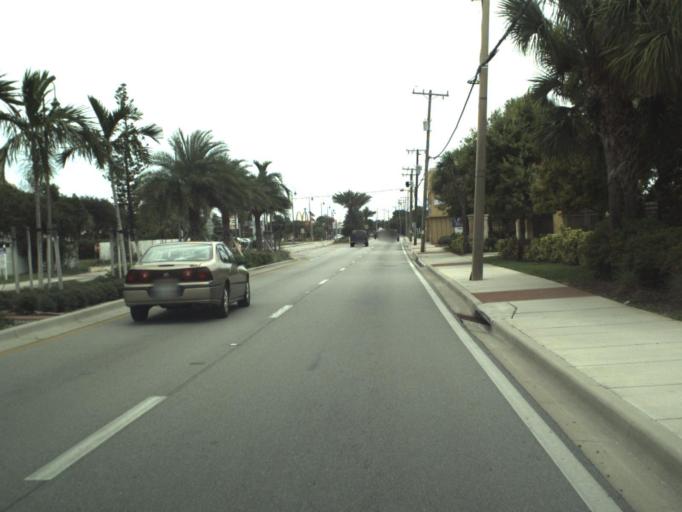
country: US
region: Florida
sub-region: Palm Beach County
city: Riviera Beach
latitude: 26.7886
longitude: -80.0545
